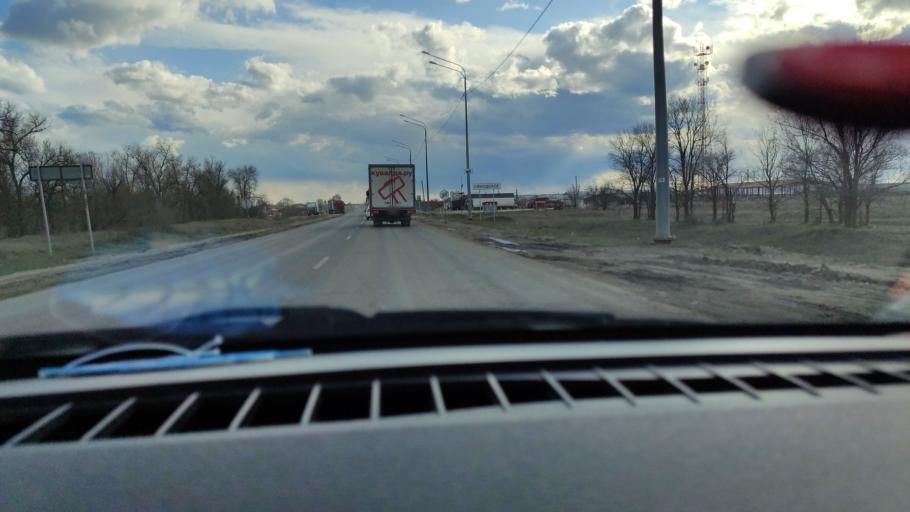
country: RU
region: Saratov
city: Sinodskoye
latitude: 51.9965
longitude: 46.6740
